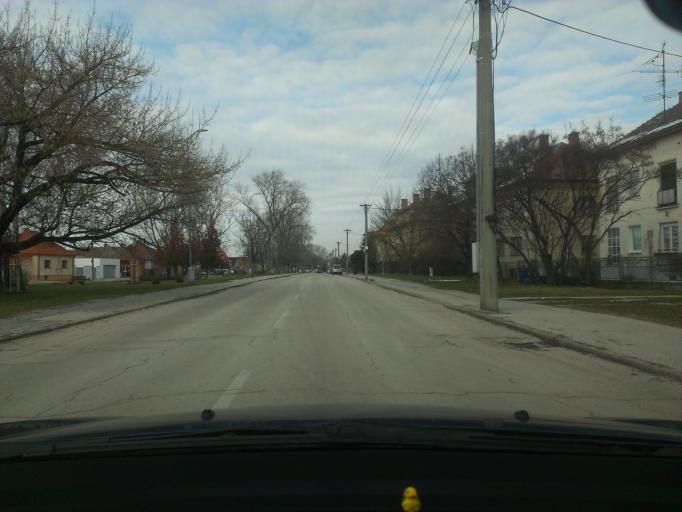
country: SK
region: Trnavsky
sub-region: Okres Trnava
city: Piestany
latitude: 48.6027
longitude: 17.8336
